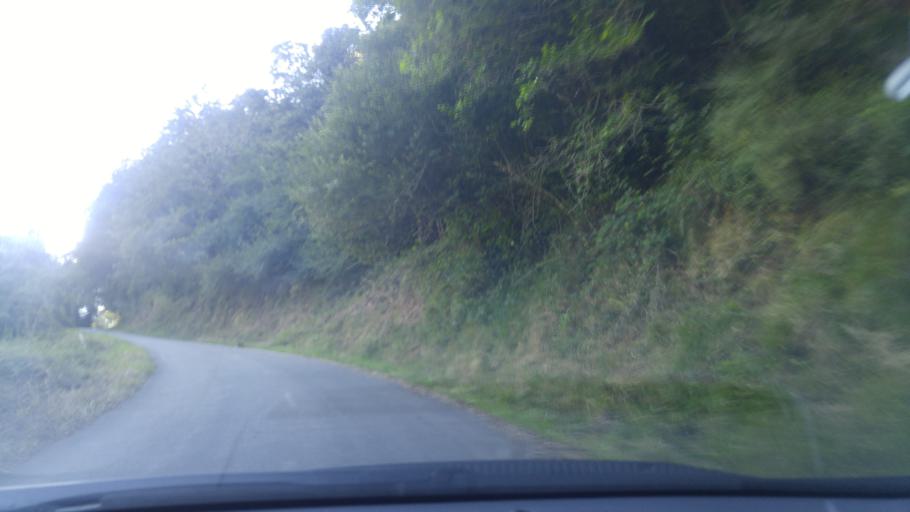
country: ES
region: Asturias
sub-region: Province of Asturias
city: Barzana
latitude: 43.1693
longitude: -5.9837
